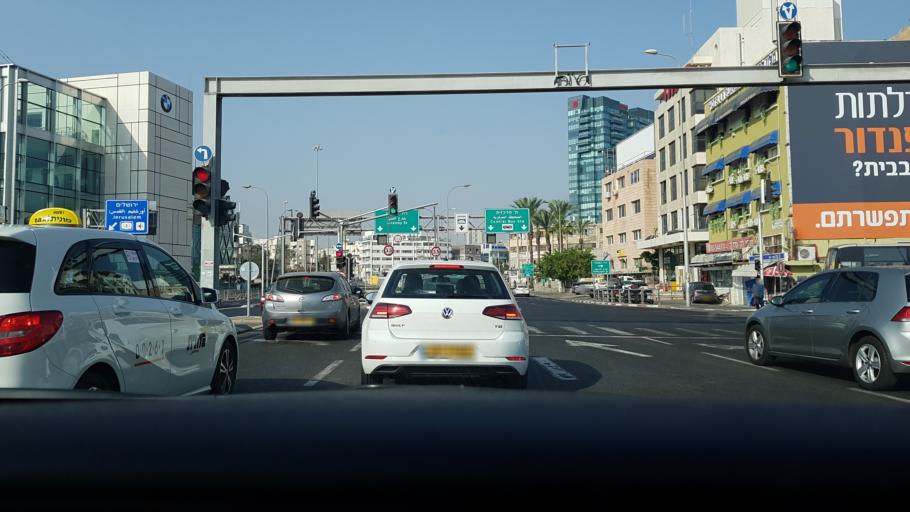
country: IL
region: Tel Aviv
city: Tel Aviv
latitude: 32.0594
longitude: 34.7861
